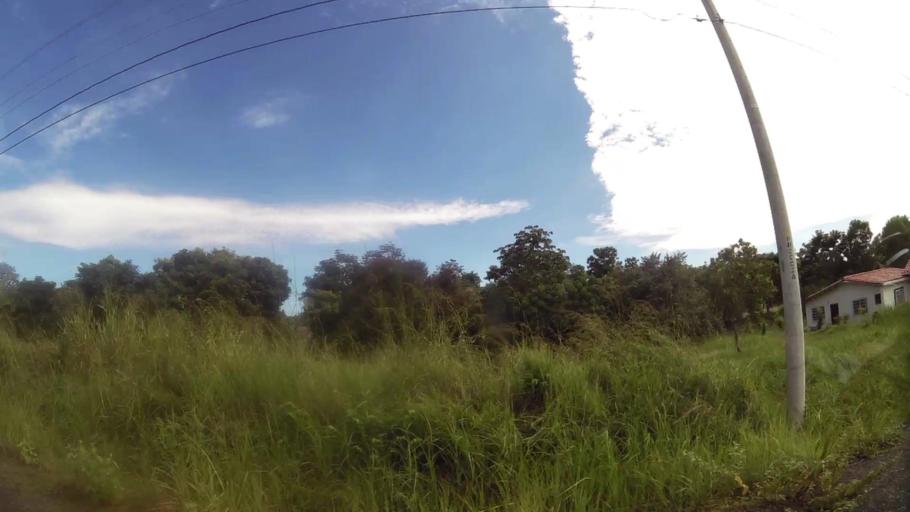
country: PA
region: Panama
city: Nueva Gorgona
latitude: 8.5389
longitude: -79.8960
